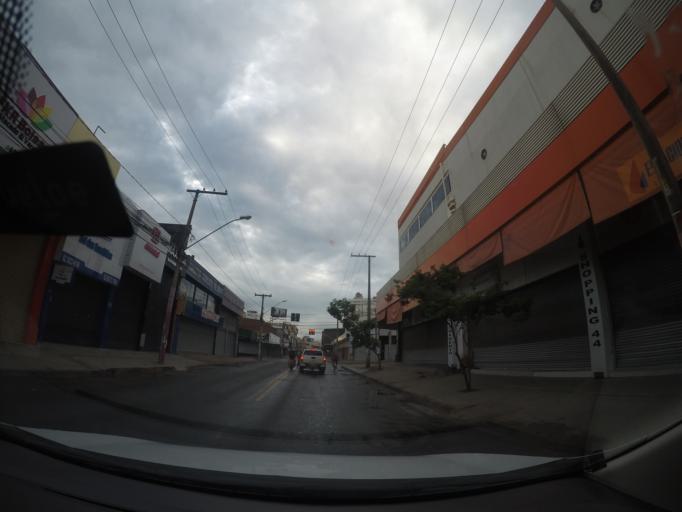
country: BR
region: Goias
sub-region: Goiania
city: Goiania
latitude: -16.6579
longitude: -49.2572
